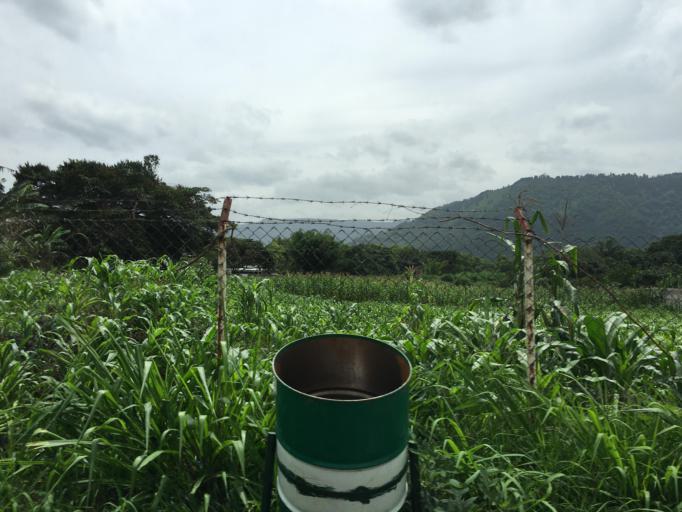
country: GT
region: Guatemala
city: Villa Canales
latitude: 14.4265
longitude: -90.5538
